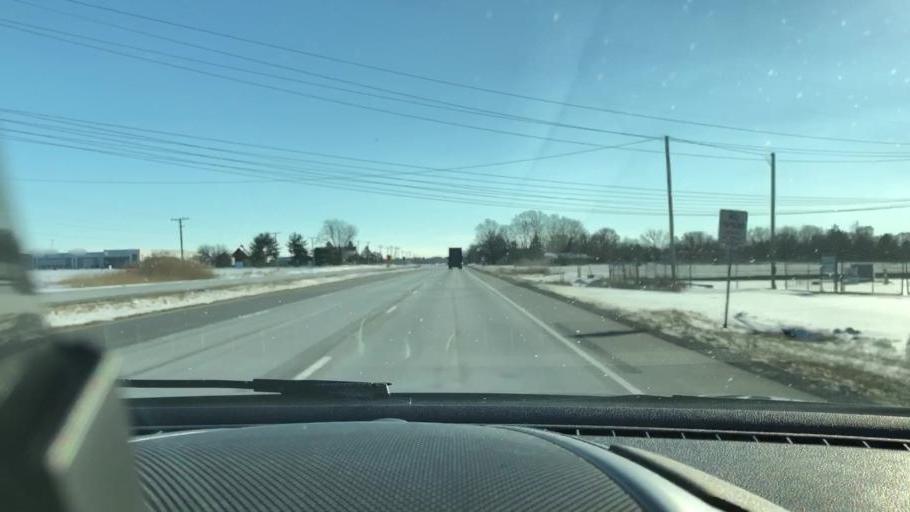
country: US
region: Illinois
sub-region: Will County
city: Preston Heights
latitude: 41.4562
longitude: -88.0794
